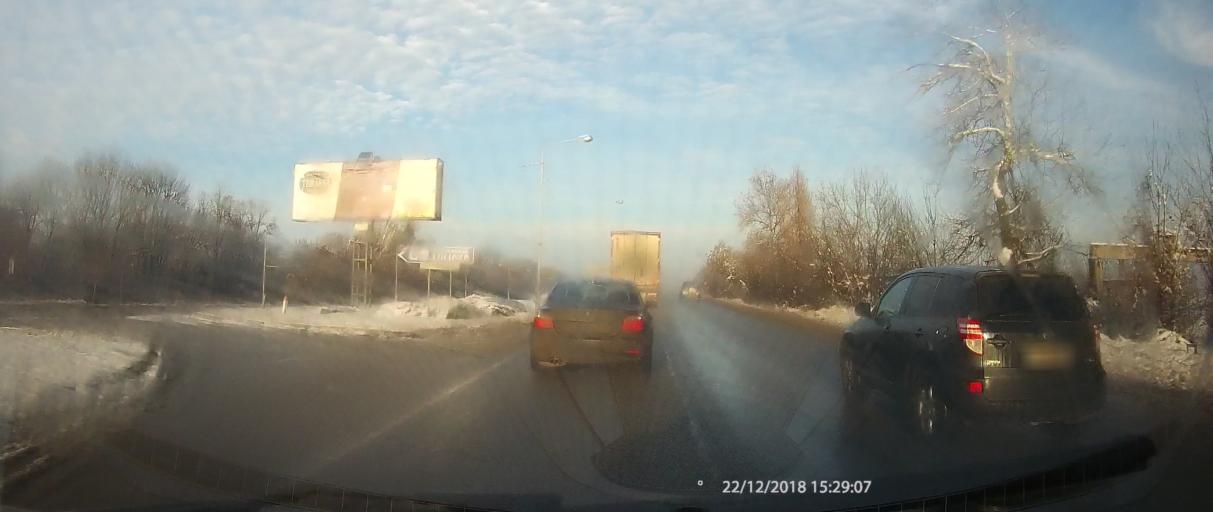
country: RO
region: Giurgiu
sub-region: Comuna Slobozia
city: Slobozia
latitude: 43.8074
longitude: 25.9233
